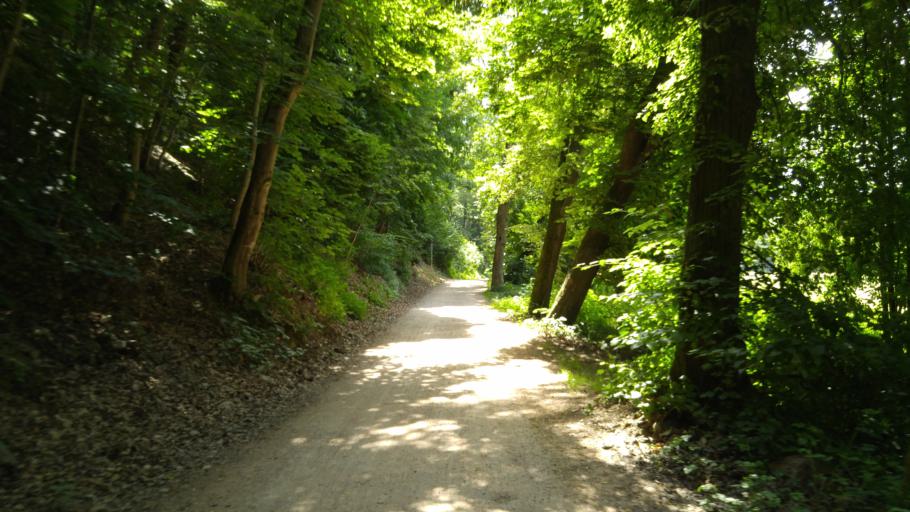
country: DE
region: Baden-Wuerttemberg
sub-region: Freiburg Region
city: Sulzburg
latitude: 47.8709
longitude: 7.7418
